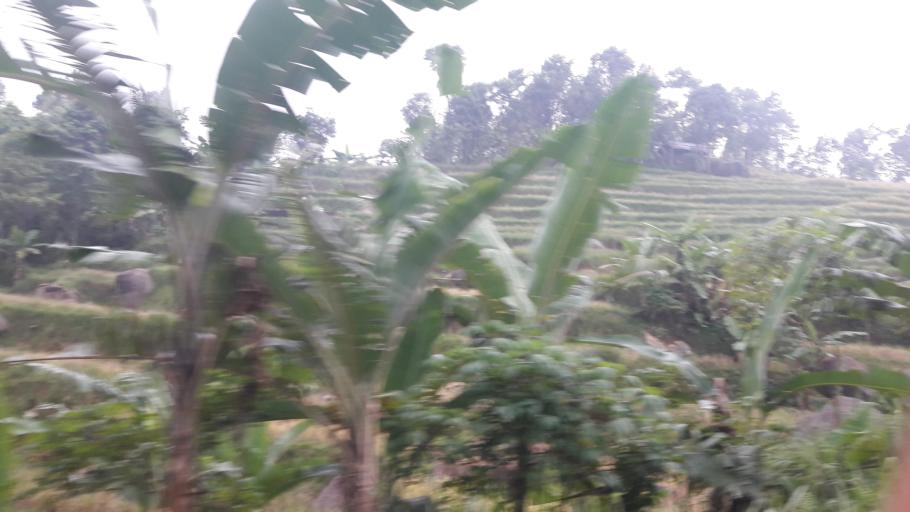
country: ID
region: West Java
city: Cipeundeuy
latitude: -6.6786
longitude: 106.5261
